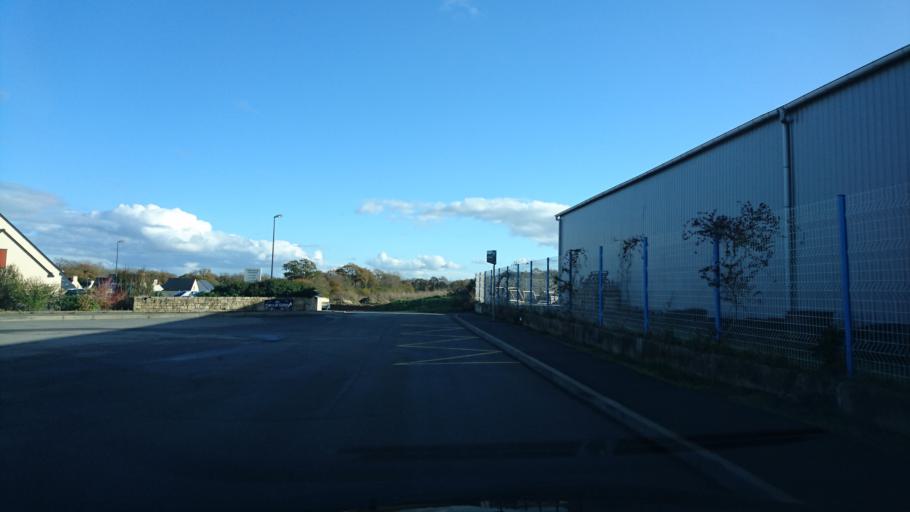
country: FR
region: Brittany
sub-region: Departement du Finistere
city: Quimperle
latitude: 47.8658
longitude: -3.5787
